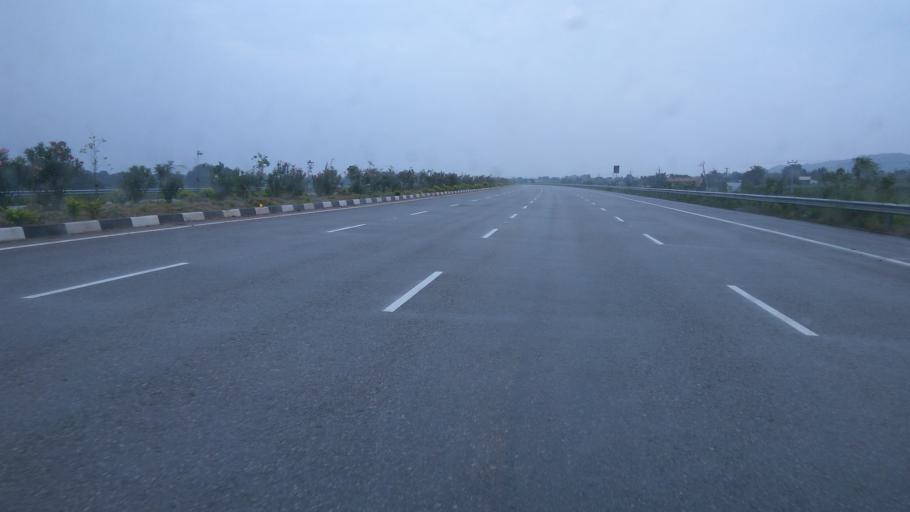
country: IN
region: Telangana
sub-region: Rangareddi
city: Ghatkesar
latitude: 17.4703
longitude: 78.6705
